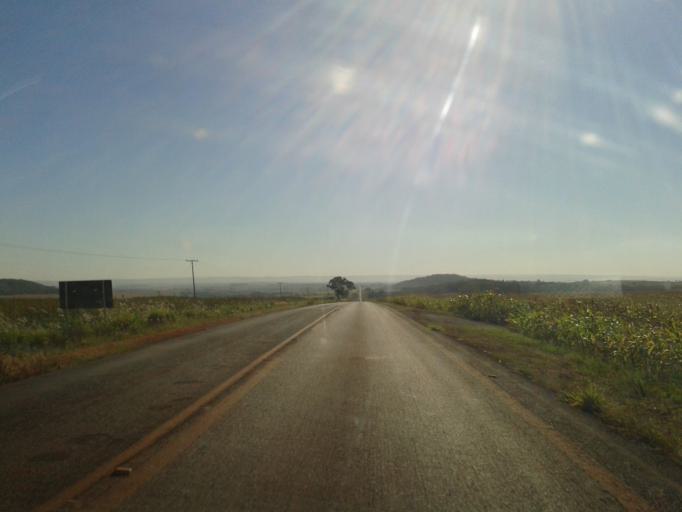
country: BR
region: Minas Gerais
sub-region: Capinopolis
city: Capinopolis
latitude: -18.6565
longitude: -49.5542
